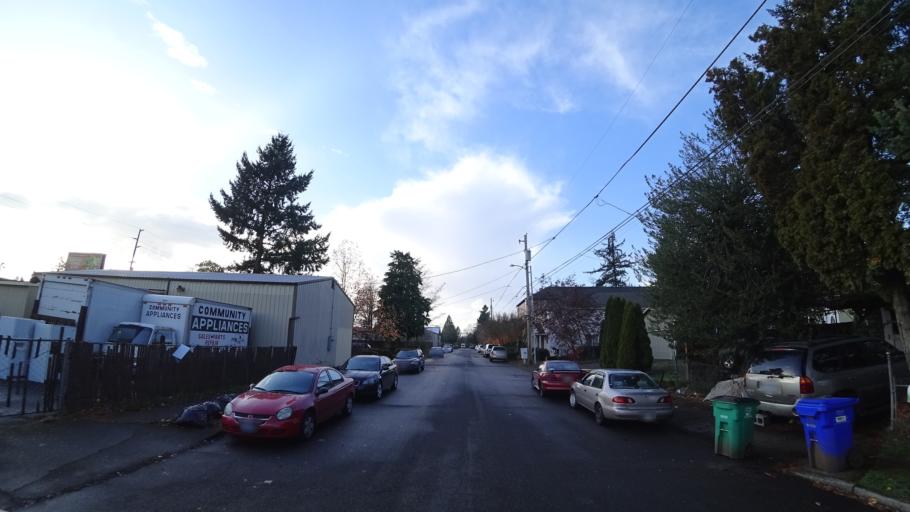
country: US
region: Oregon
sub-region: Multnomah County
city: Lents
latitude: 45.5197
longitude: -122.5389
